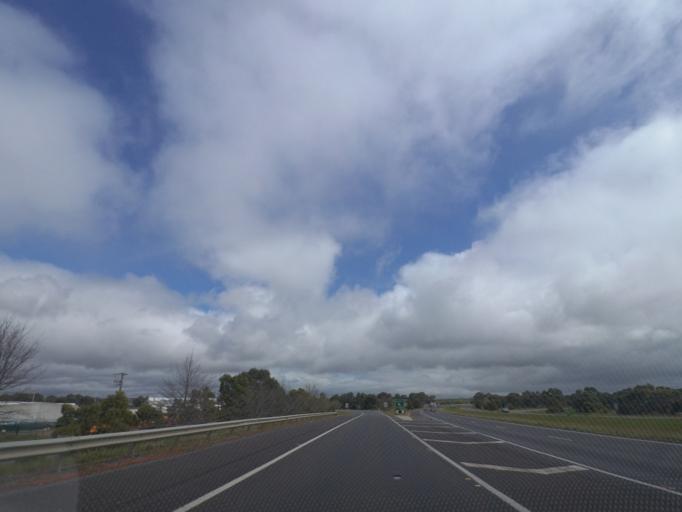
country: AU
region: Victoria
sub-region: Ballarat North
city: Lake Wendouree
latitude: -37.5212
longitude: 143.8491
